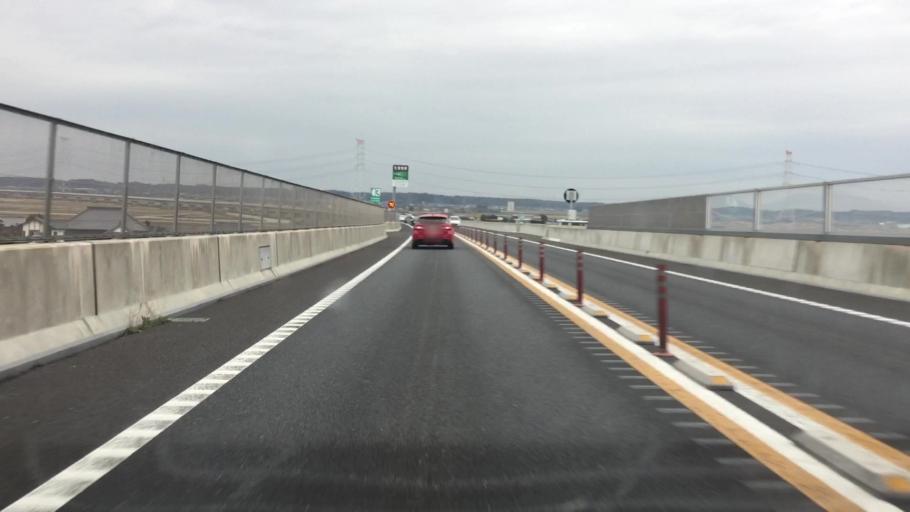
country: JP
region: Ibaraki
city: Inashiki
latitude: 35.9053
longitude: 140.3739
